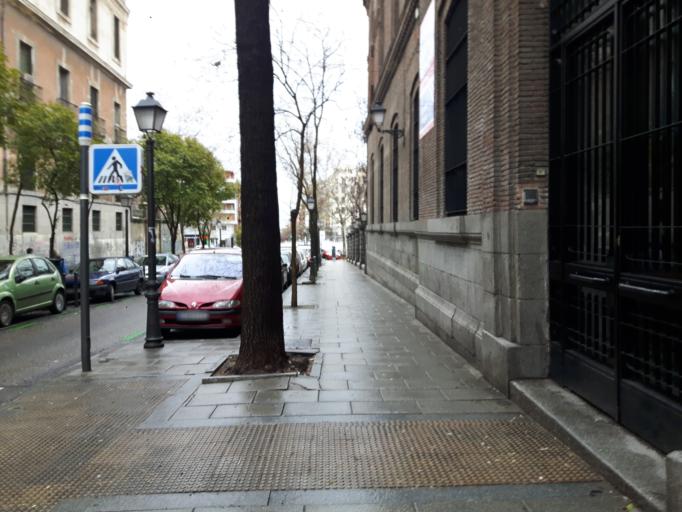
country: ES
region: Madrid
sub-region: Provincia de Madrid
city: Arganzuela
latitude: 40.4061
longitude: -3.7031
